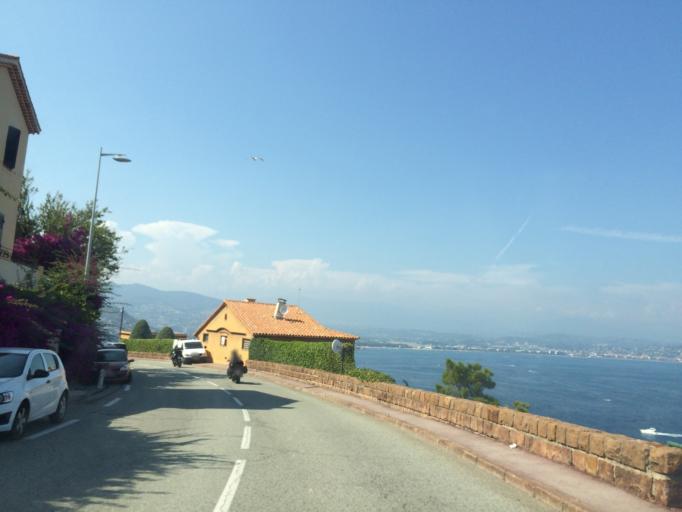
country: FR
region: Provence-Alpes-Cote d'Azur
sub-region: Departement des Alpes-Maritimes
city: Theoule-sur-Mer
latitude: 43.5040
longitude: 6.9535
